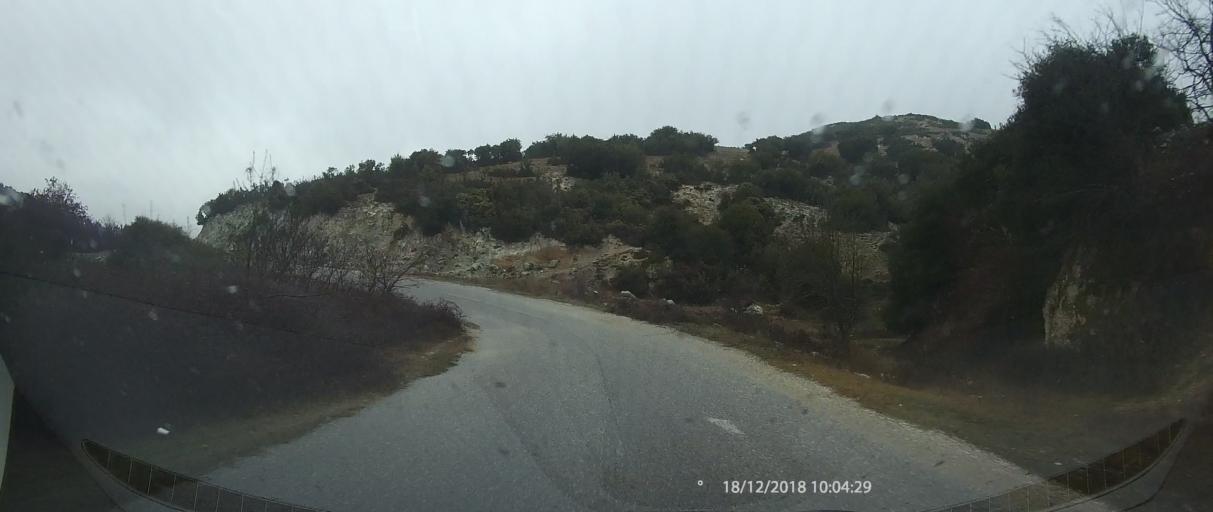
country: GR
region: Thessaly
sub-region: Nomos Larisis
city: Livadi
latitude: 40.0532
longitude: 22.2226
